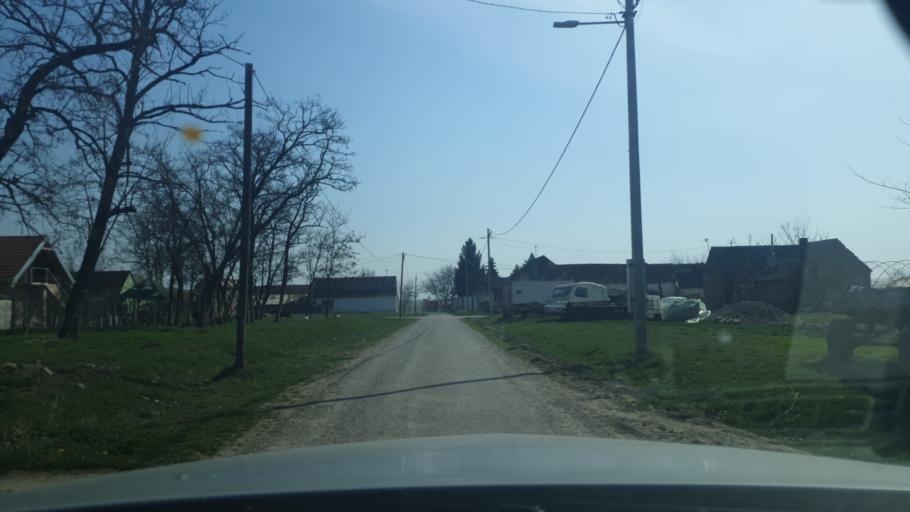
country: RS
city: Putinci
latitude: 45.0405
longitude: 19.9399
